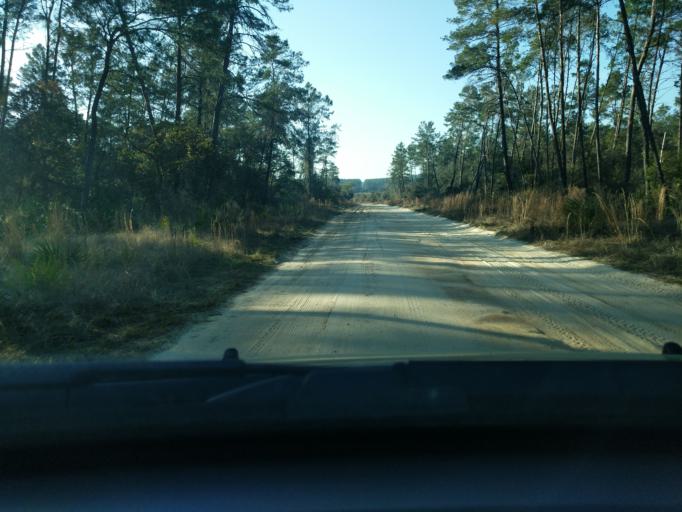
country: US
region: Florida
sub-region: Marion County
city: Silver Springs Shores
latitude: 29.2213
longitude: -81.8276
